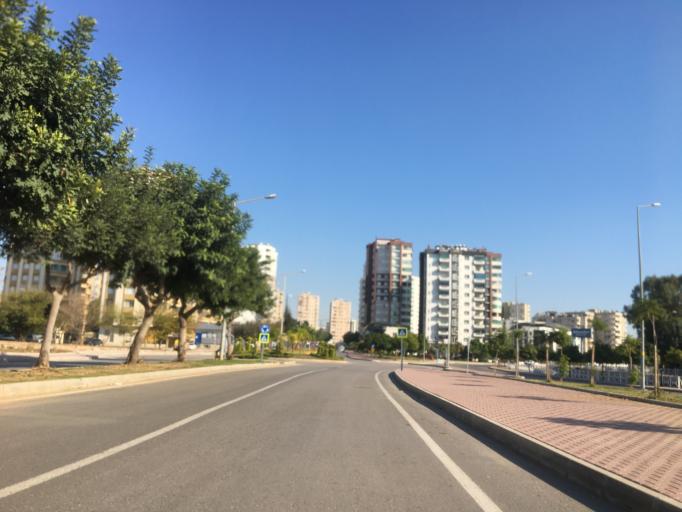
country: TR
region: Adana
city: Seyhan
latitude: 37.0289
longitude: 35.2696
